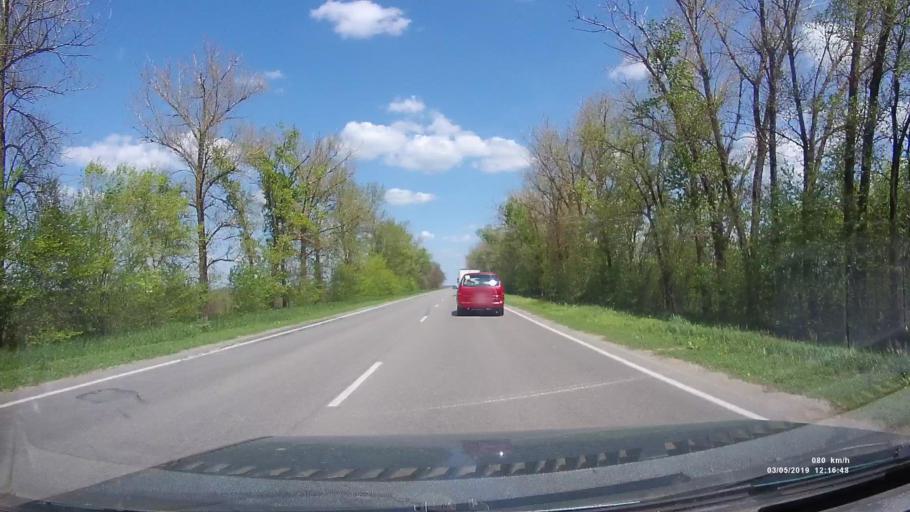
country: RU
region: Rostov
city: Melikhovskaya
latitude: 47.3764
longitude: 40.5876
